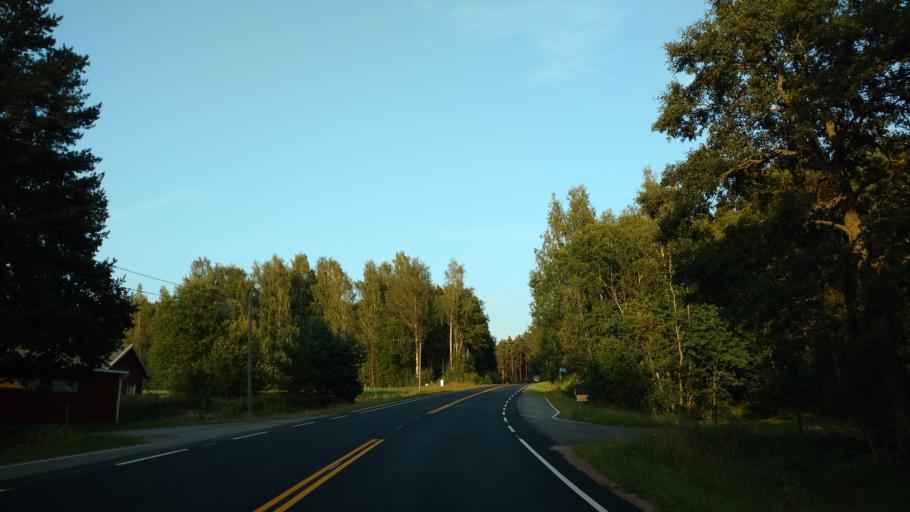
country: FI
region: Varsinais-Suomi
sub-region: Aboland-Turunmaa
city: Kimito
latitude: 60.1803
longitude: 22.8347
